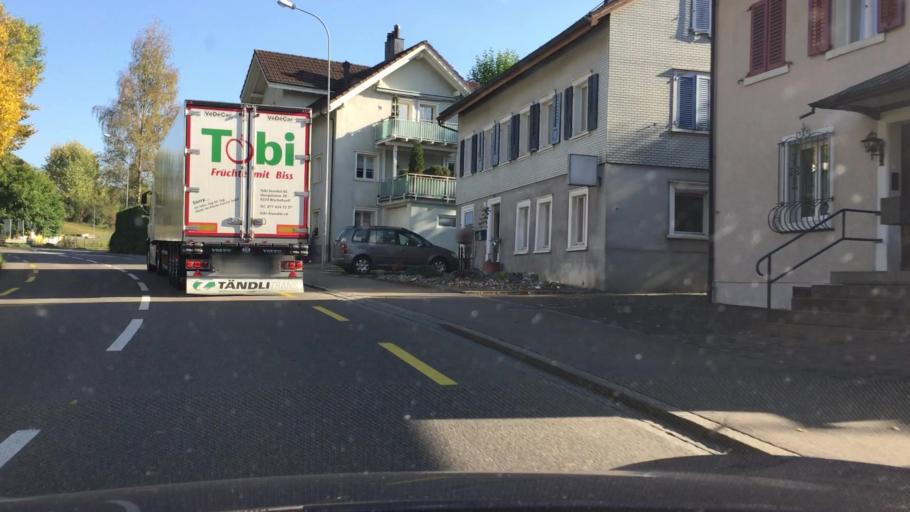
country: CH
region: Saint Gallen
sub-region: Wahlkreis St. Gallen
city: Waldkirch
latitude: 47.4779
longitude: 9.2513
